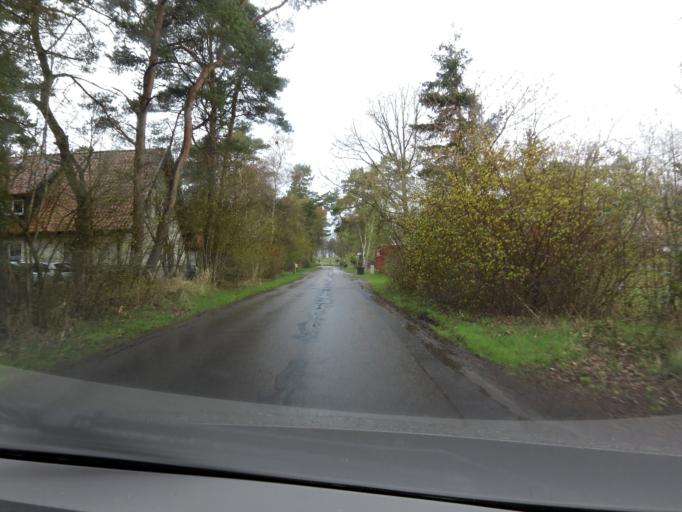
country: DE
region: Mecklenburg-Vorpommern
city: Zingst
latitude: 54.4393
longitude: 12.7224
